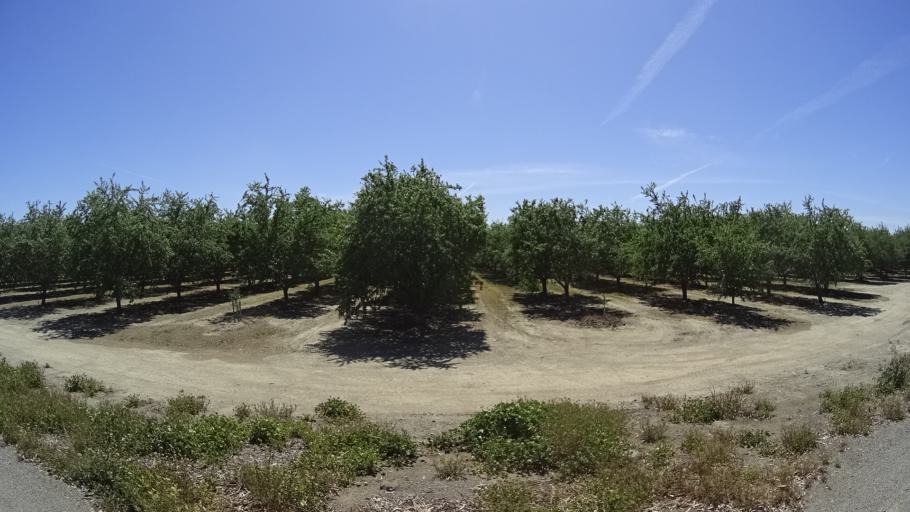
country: US
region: California
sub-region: Glenn County
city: Hamilton City
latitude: 39.7215
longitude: -122.0902
